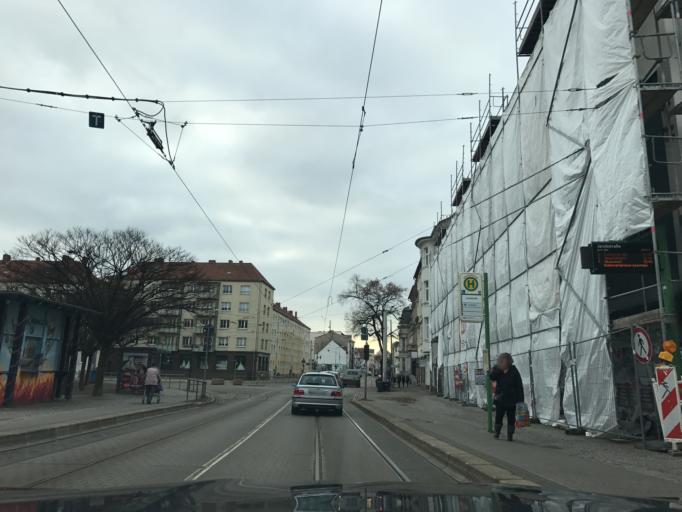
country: DE
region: Brandenburg
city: Brandenburg an der Havel
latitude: 52.4053
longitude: 12.5577
